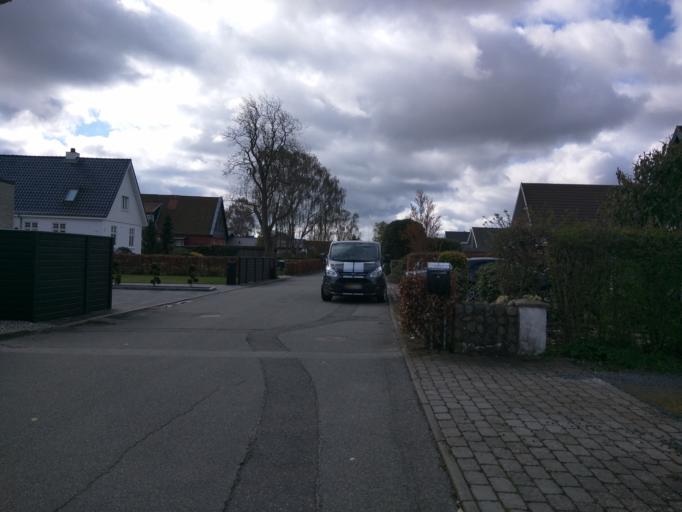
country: DK
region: South Denmark
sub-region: Fredericia Kommune
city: Snoghoj
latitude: 55.5485
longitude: 9.7279
